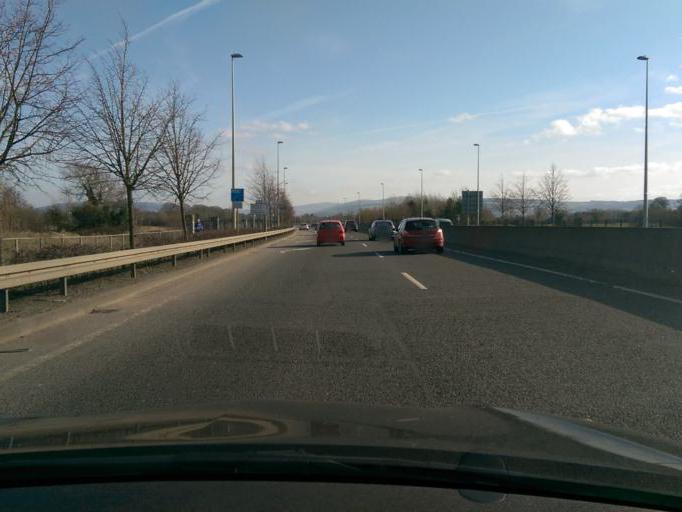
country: IE
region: Leinster
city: Clondalkin
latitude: 53.3186
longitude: -6.4287
